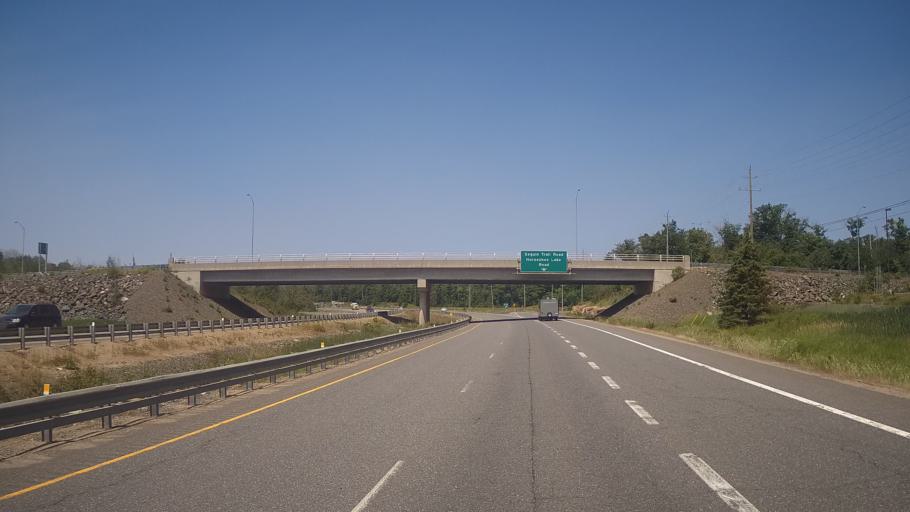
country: CA
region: Ontario
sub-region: Parry Sound District
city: Parry Sound
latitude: 45.3052
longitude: -79.8958
